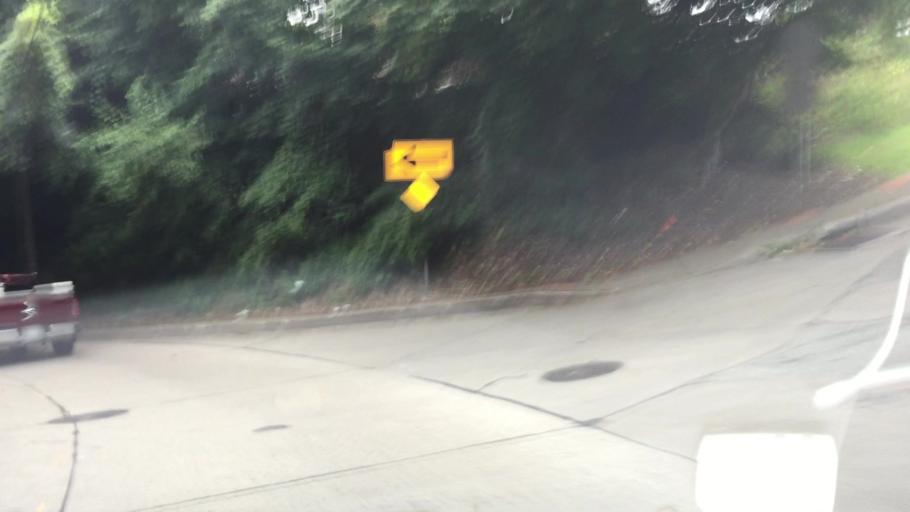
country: US
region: Pennsylvania
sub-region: Allegheny County
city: Carnegie
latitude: 40.4082
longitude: -80.0773
